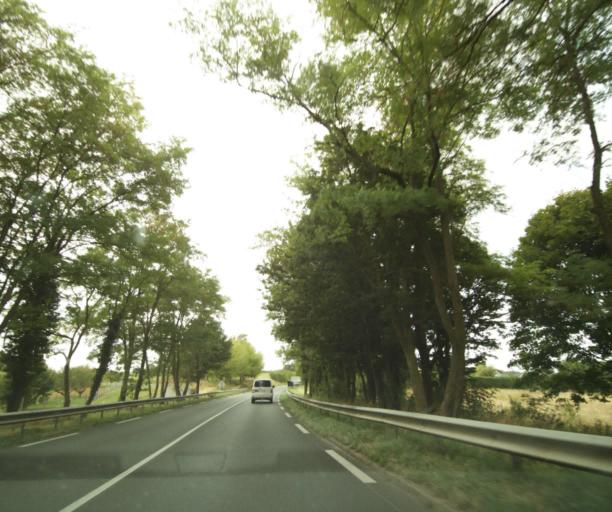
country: FR
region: Centre
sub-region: Departement d'Indre-et-Loire
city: Loches
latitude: 47.1103
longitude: 0.9840
